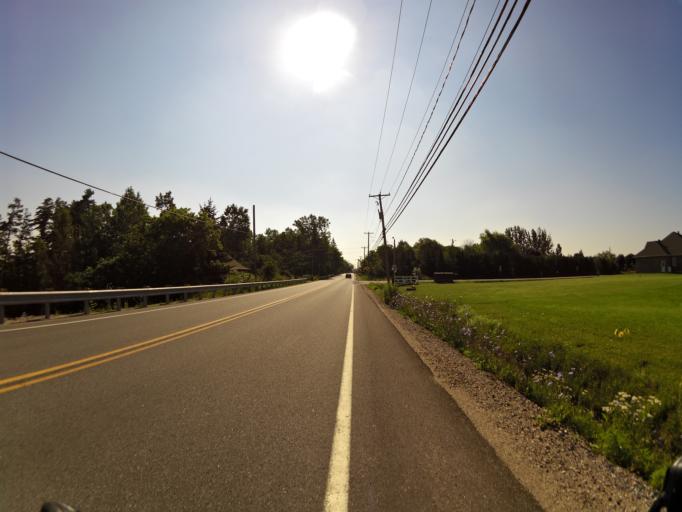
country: CA
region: Quebec
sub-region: Outaouais
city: Gatineau
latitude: 45.4908
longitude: -75.7653
